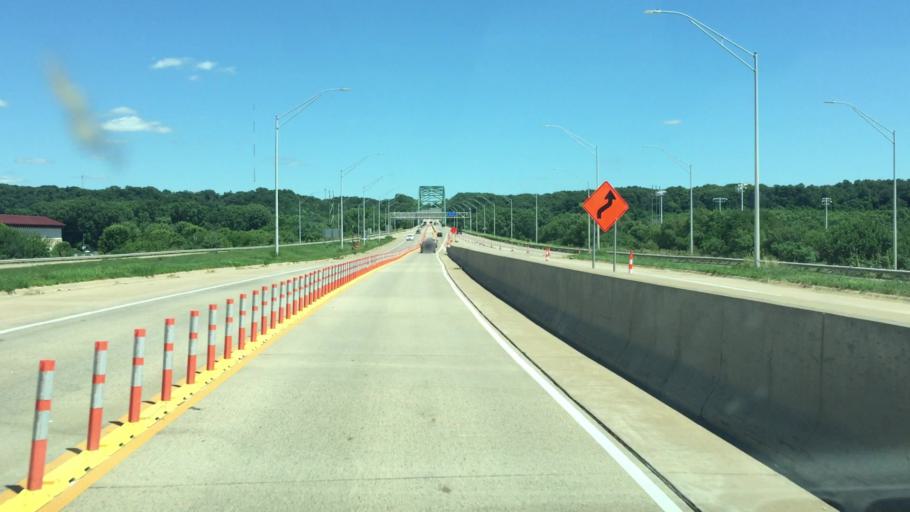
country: US
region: Iowa
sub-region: Dubuque County
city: Dubuque
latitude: 42.5158
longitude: -90.6469
